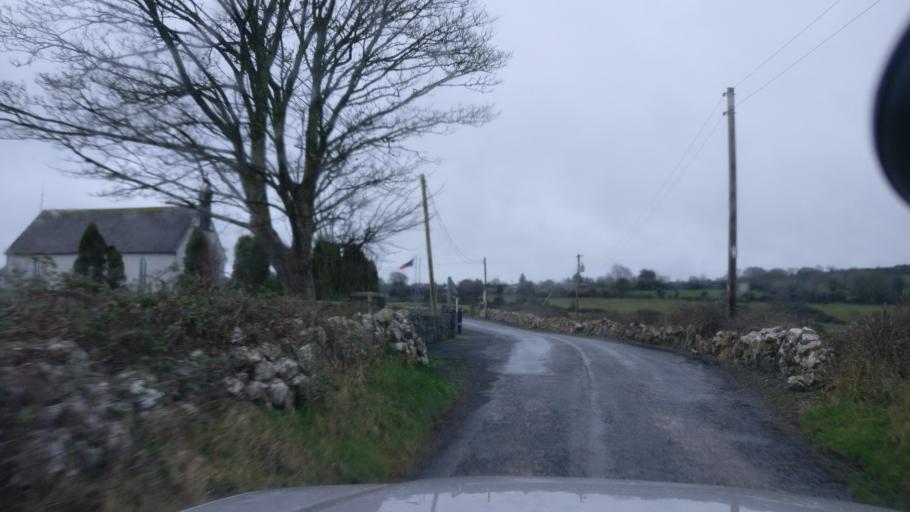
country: IE
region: Connaught
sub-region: County Galway
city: Loughrea
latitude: 53.1750
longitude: -8.6495
